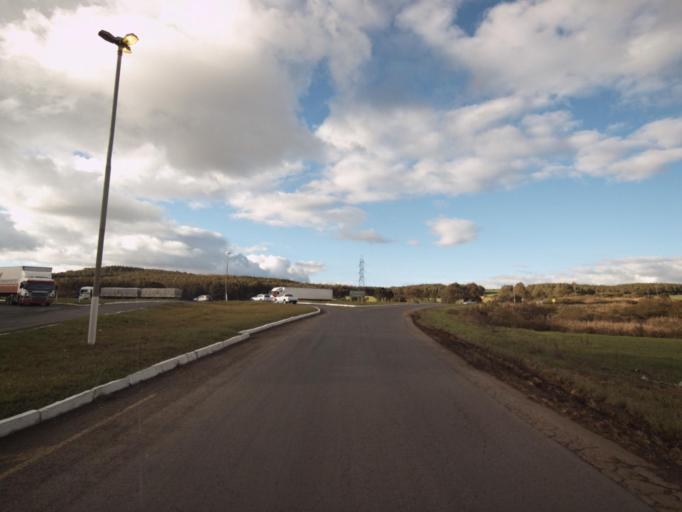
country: BR
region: Santa Catarina
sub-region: Campos Novos
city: Campos Novos
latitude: -27.3943
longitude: -51.1925
